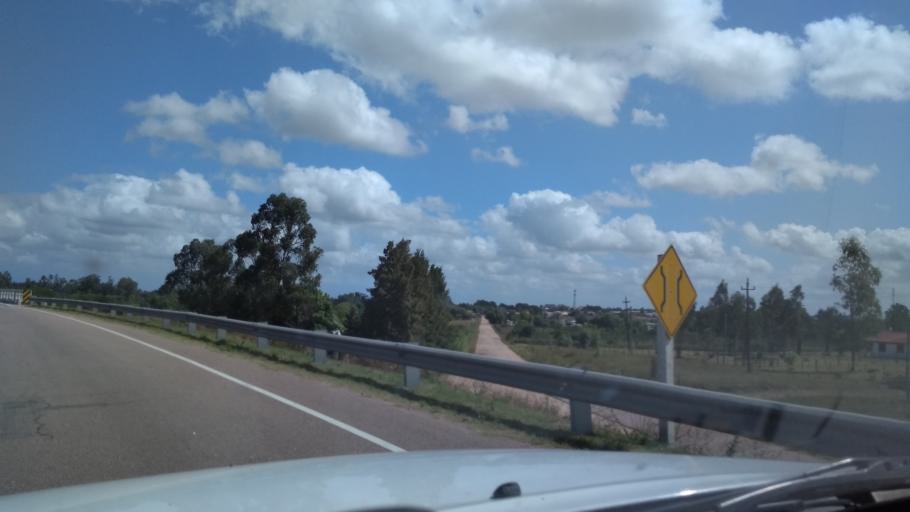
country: UY
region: Canelones
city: Sauce
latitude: -34.6386
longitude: -56.0528
